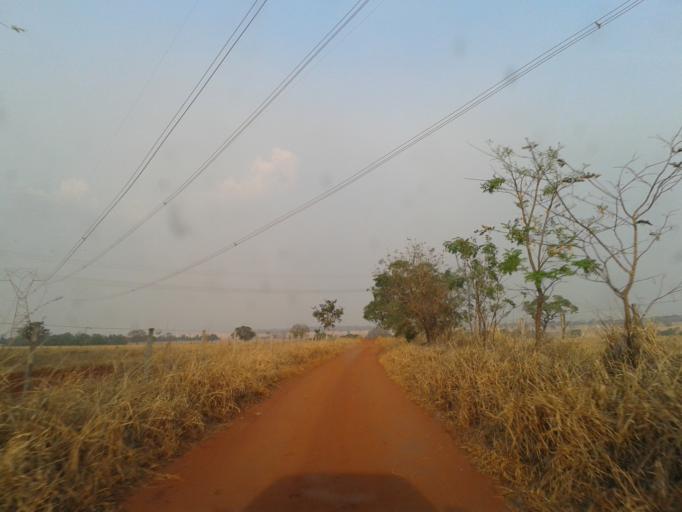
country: BR
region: Minas Gerais
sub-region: Capinopolis
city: Capinopolis
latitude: -18.8069
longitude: -49.7409
